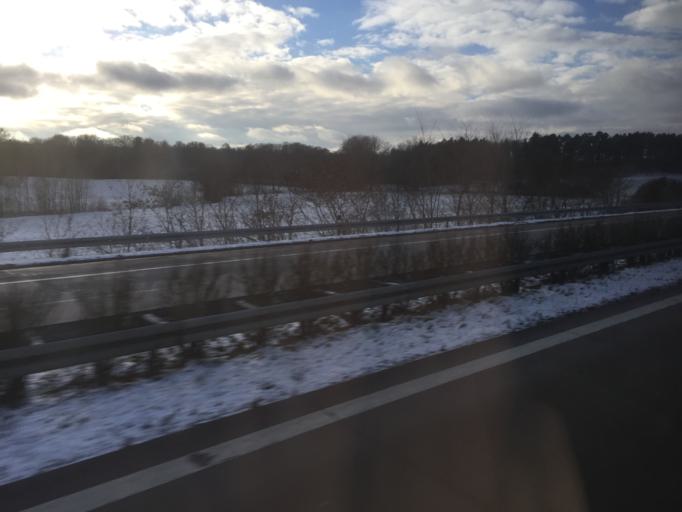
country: DE
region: Mecklenburg-Vorpommern
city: Siggelkow
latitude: 53.2991
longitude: 11.9425
